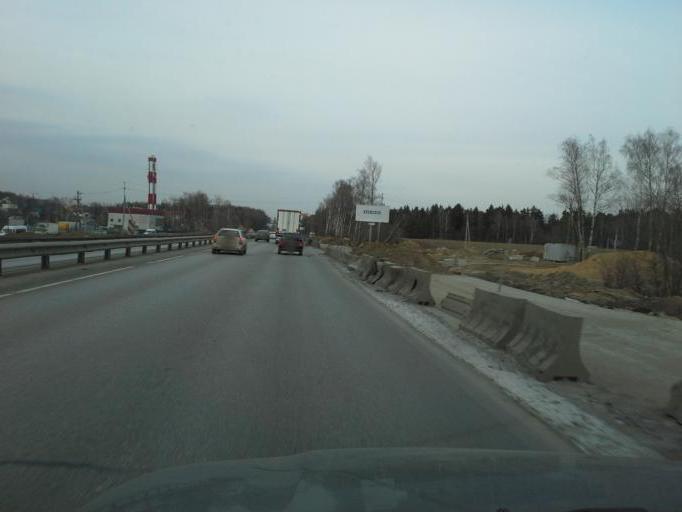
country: RU
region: Moskovskaya
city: Odintsovo
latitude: 55.6617
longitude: 37.3028
